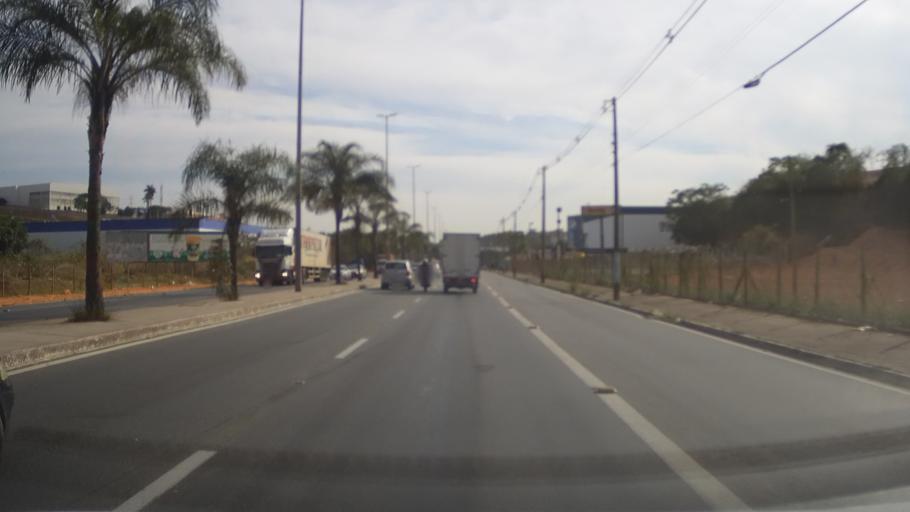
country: BR
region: Minas Gerais
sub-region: Contagem
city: Contagem
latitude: -19.9134
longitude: -44.0523
